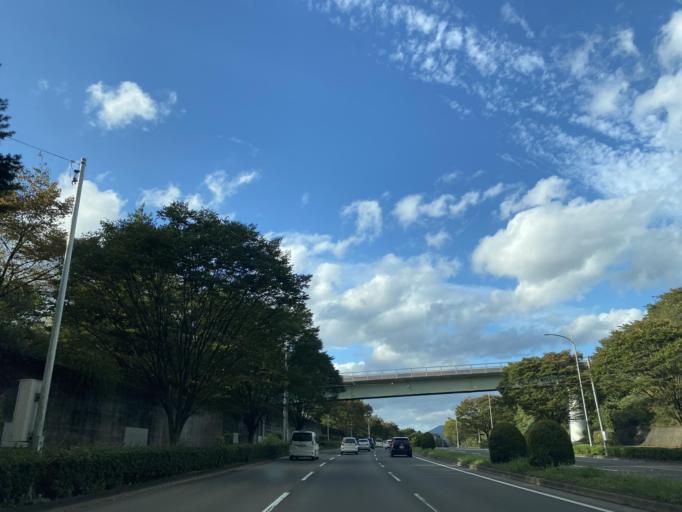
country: JP
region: Miyagi
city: Sendai-shi
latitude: 38.3125
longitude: 140.8458
